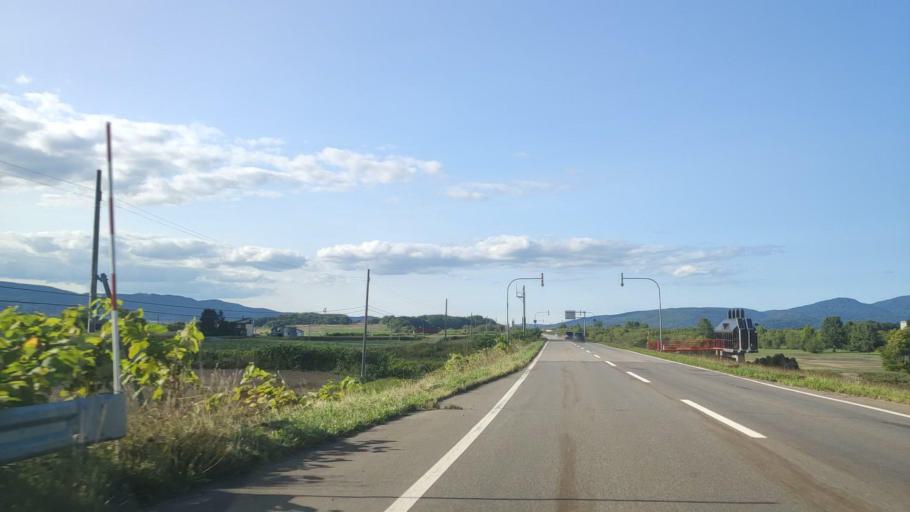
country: JP
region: Hokkaido
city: Nayoro
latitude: 44.8041
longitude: 142.0674
